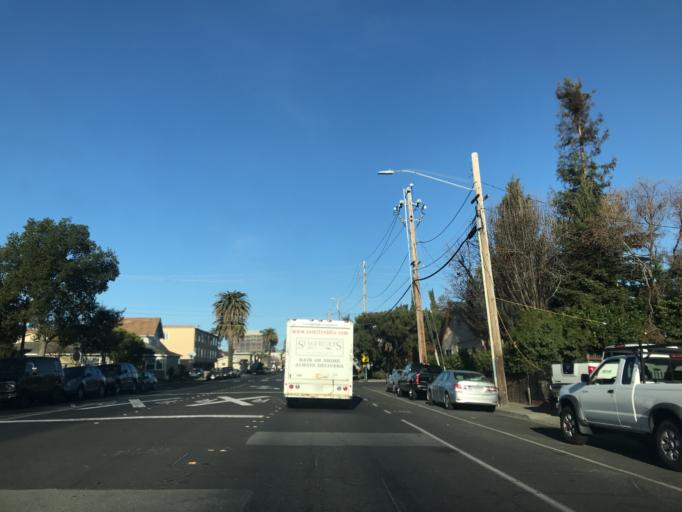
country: US
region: California
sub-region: San Mateo County
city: Redwood City
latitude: 37.4823
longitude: -122.2218
